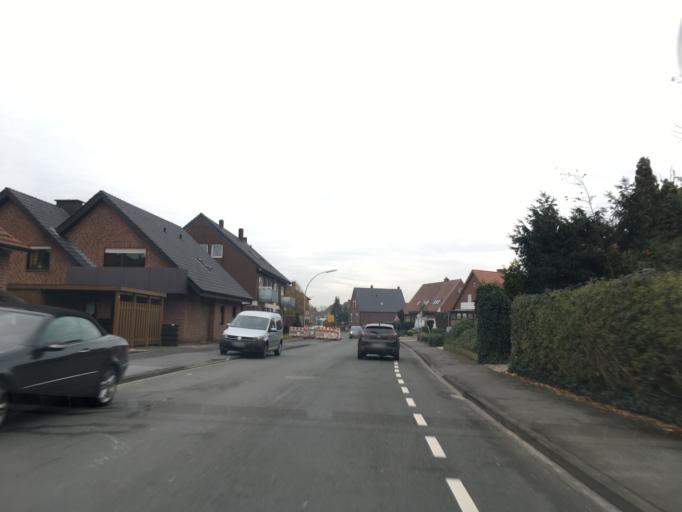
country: DE
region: North Rhine-Westphalia
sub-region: Regierungsbezirk Munster
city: Telgte
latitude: 51.9771
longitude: 7.7830
